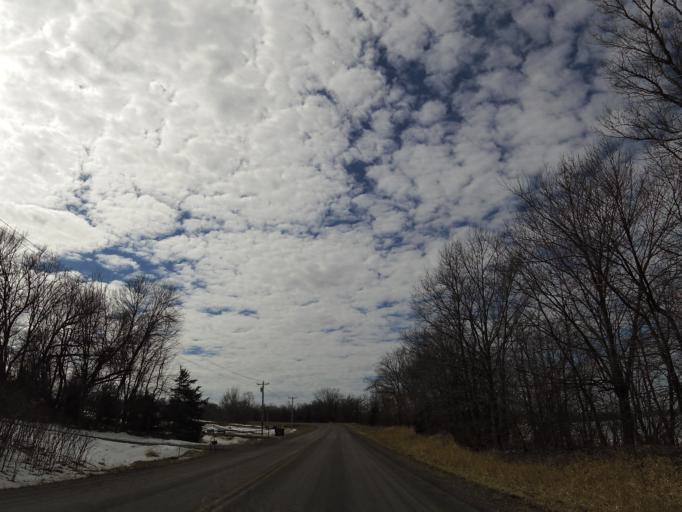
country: US
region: Minnesota
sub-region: Le Sueur County
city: New Prague
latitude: 44.6049
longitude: -93.5552
